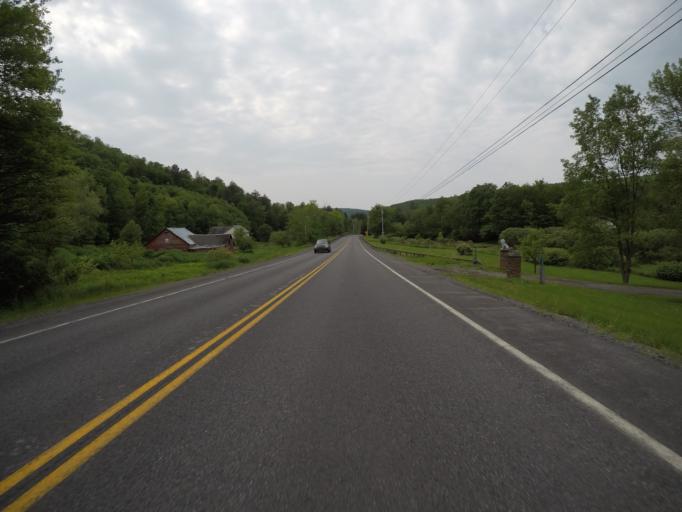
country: US
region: New York
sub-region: Sullivan County
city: Livingston Manor
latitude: 41.9898
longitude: -74.8937
